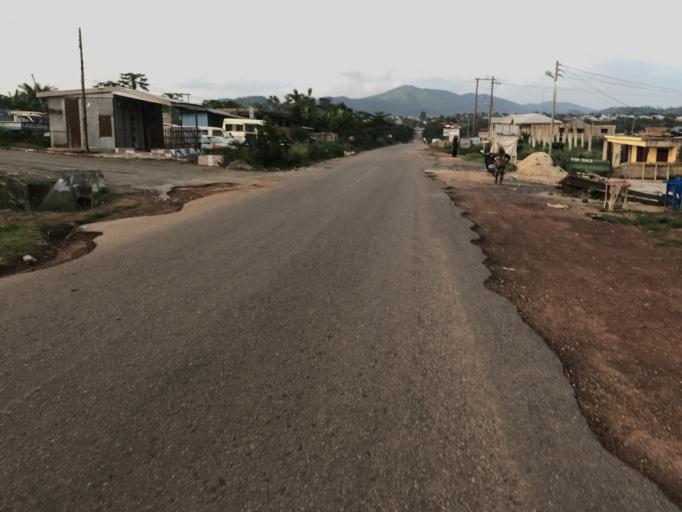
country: GH
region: Ashanti
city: Obuasi
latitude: 6.2051
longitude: -1.6014
